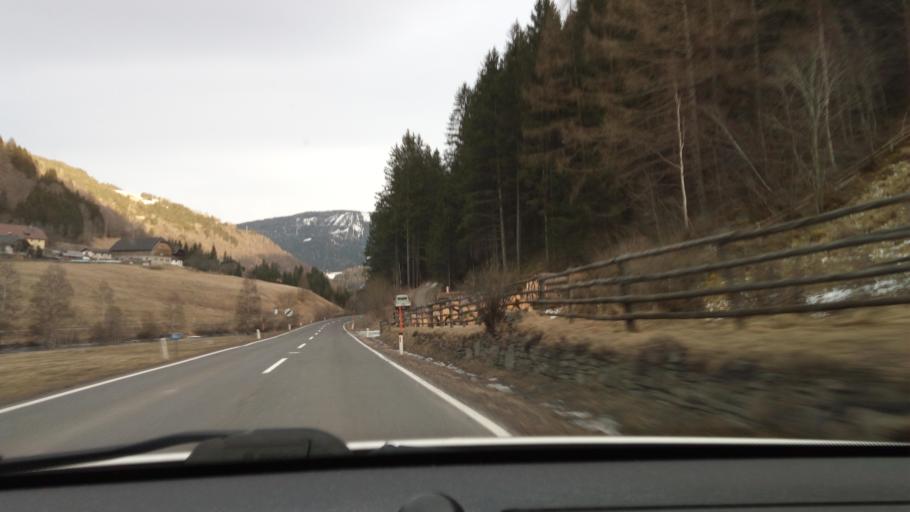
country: AT
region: Salzburg
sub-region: Politischer Bezirk Tamsweg
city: Ramingstein
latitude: 47.0731
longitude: 13.8599
